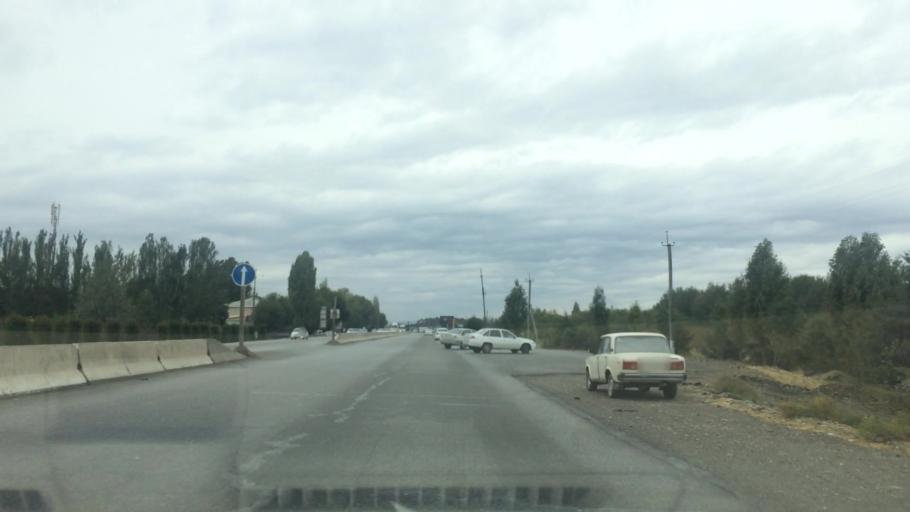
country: UZ
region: Jizzax
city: Jizzax
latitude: 40.0140
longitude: 67.6041
